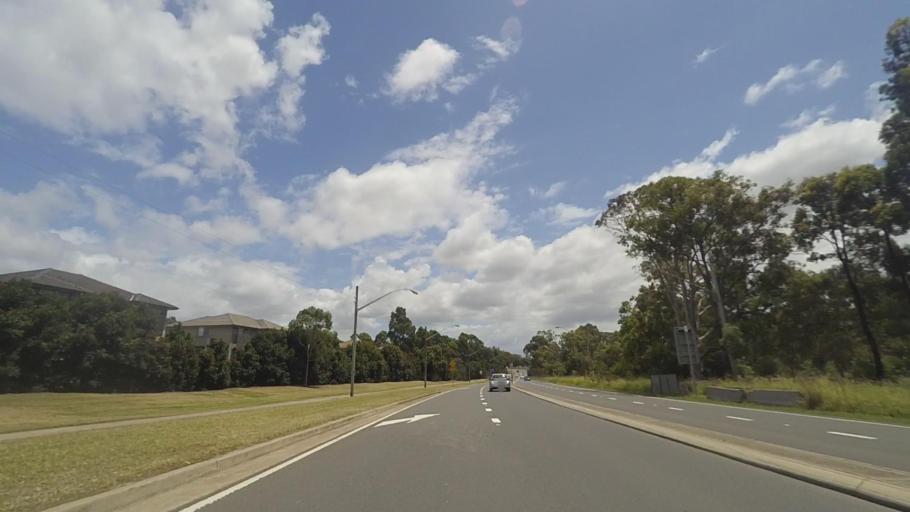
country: AU
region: New South Wales
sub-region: Liverpool
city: Holsworthy
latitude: -33.9605
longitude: 150.9591
